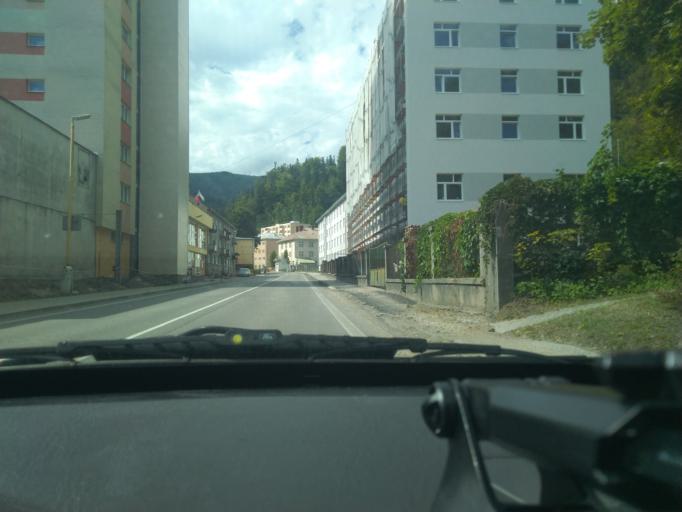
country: SK
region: Banskobystricky
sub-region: Okres Banska Bystrica
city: Banska Bystrica
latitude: 48.7957
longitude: 19.0769
